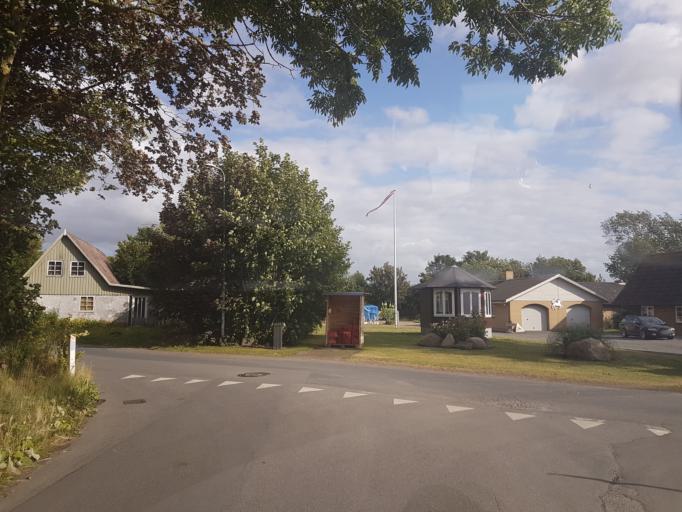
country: DK
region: South Denmark
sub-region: Middelfart Kommune
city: Brenderup
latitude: 55.5300
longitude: 10.0089
